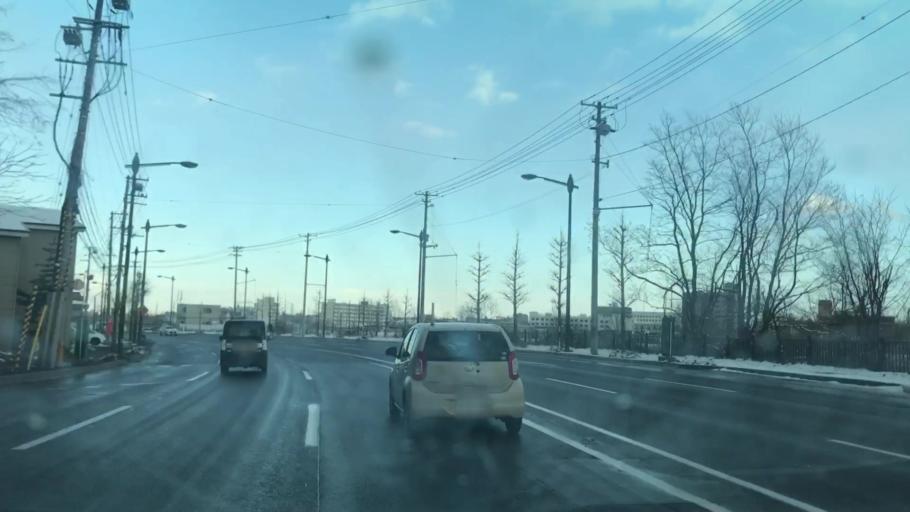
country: JP
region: Hokkaido
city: Sapporo
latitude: 43.0029
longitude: 141.3421
